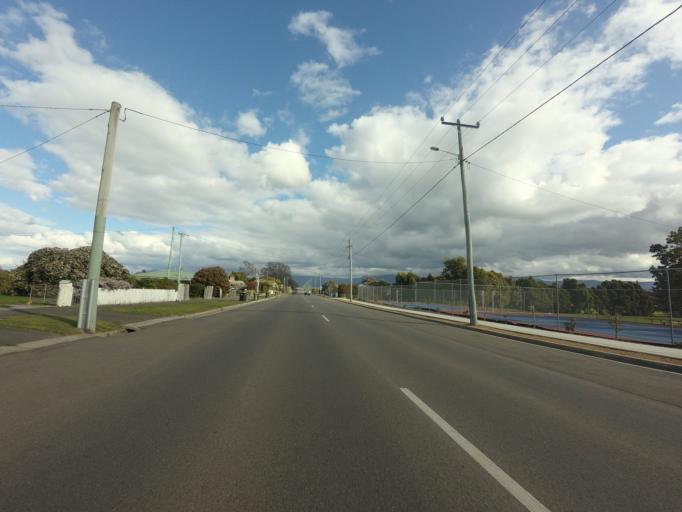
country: AU
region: Tasmania
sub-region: Northern Midlands
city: Longford
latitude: -41.6916
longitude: 147.0791
